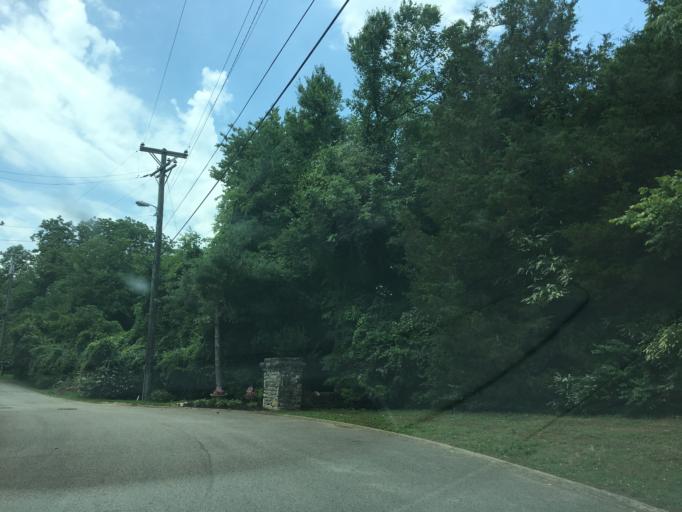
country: US
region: Tennessee
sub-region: Davidson County
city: Oak Hill
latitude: 36.0997
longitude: -86.8114
